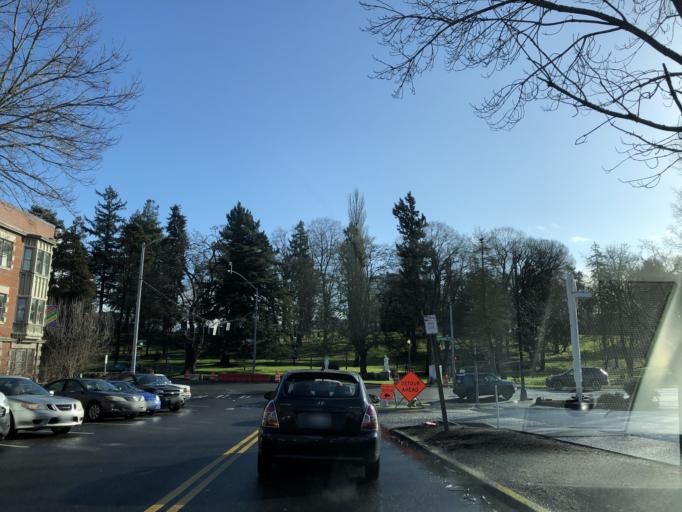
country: US
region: Washington
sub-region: Pierce County
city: Tacoma
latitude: 47.2630
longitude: -122.4505
